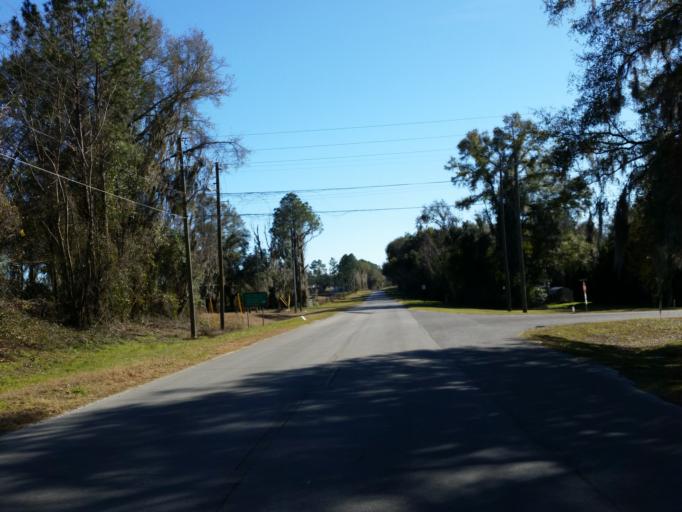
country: US
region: Florida
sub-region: Hamilton County
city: Jasper
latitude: 30.5058
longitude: -82.9530
